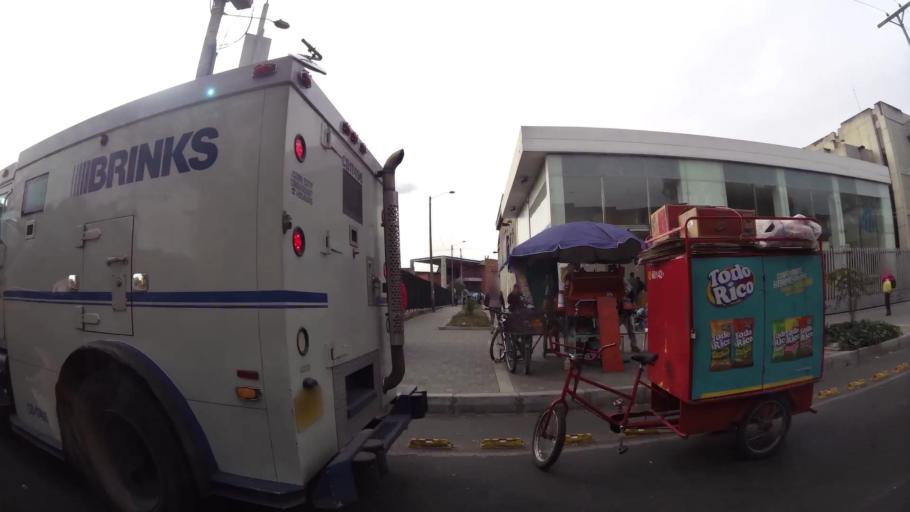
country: CO
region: Bogota D.C.
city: Bogota
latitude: 4.6251
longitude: -74.1532
